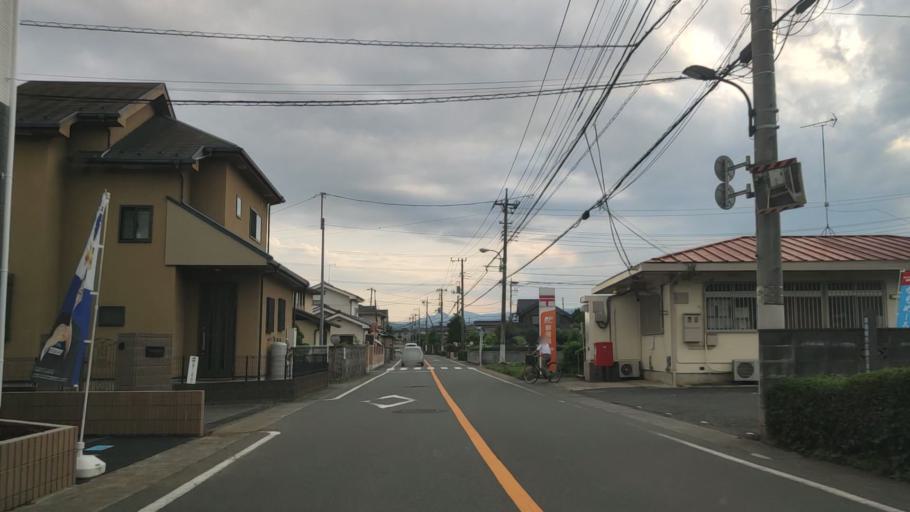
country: JP
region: Saitama
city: Hanno
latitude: 35.8027
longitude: 139.3035
